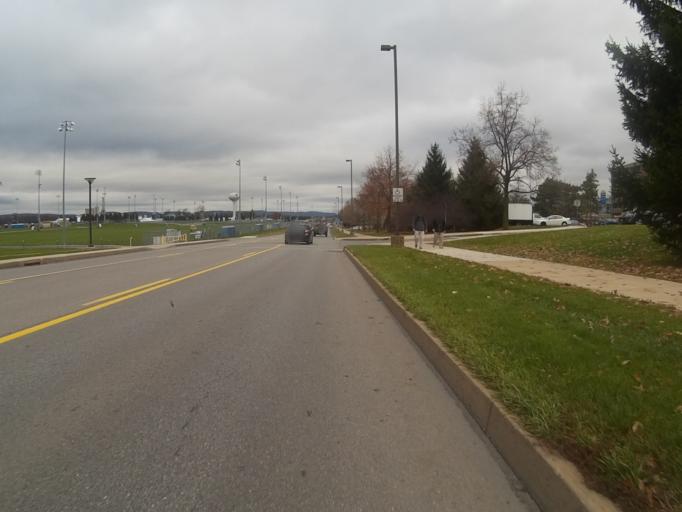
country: US
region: Pennsylvania
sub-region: Centre County
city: State College
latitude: 40.8072
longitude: -77.8638
